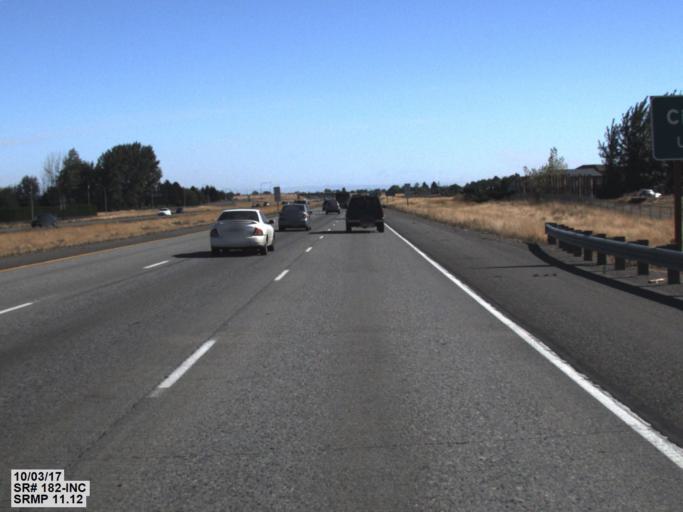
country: US
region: Washington
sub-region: Franklin County
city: West Pasco
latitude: 46.2549
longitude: -119.1481
